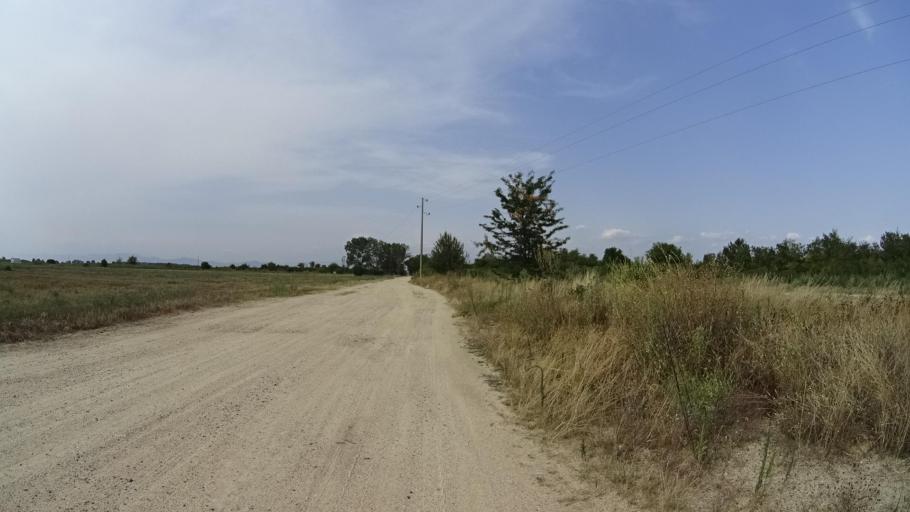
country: BG
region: Plovdiv
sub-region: Obshtina Kaloyanovo
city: Kaloyanovo
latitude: 42.3025
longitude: 24.7991
